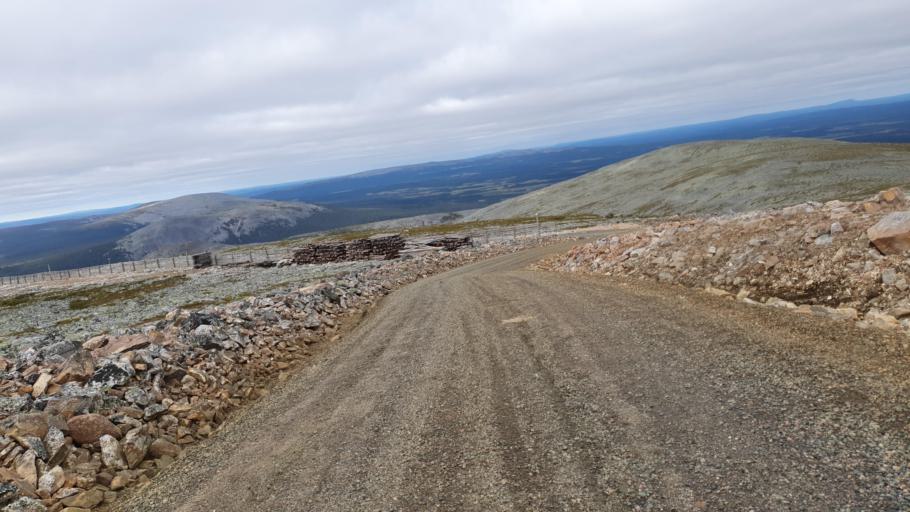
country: FI
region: Lapland
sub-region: Tunturi-Lappi
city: Kolari
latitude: 67.5689
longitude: 24.2108
